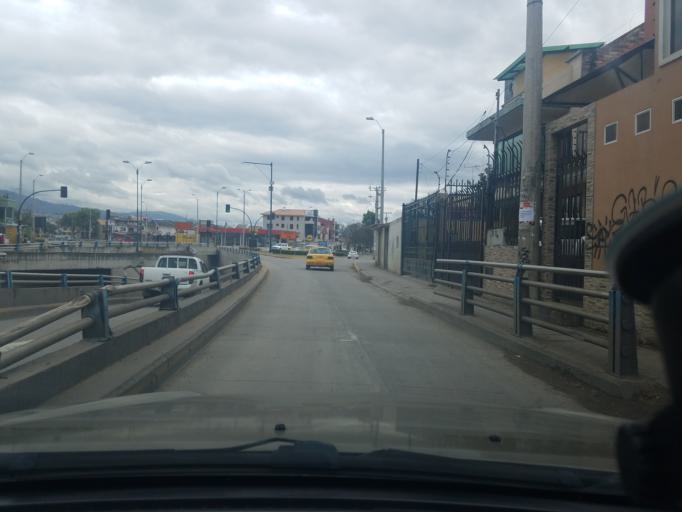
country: EC
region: Azuay
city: Cuenca
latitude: -2.9232
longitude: -79.0389
